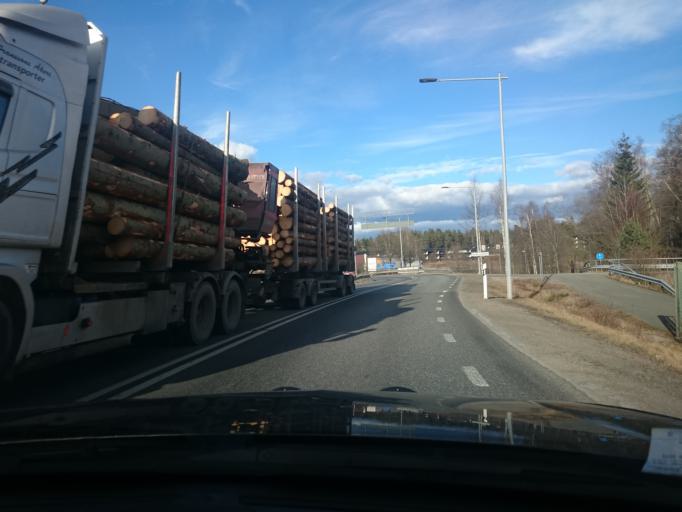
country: SE
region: Joenkoeping
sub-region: Vetlanda Kommun
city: Vetlanda
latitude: 57.4138
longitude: 15.0915
